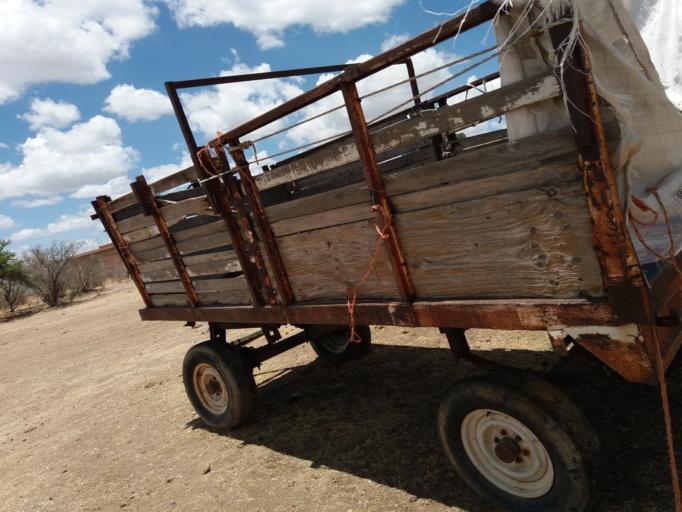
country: MX
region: Aguascalientes
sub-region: Aguascalientes
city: San Sebastian [Fraccionamiento]
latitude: 21.7795
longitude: -102.2626
